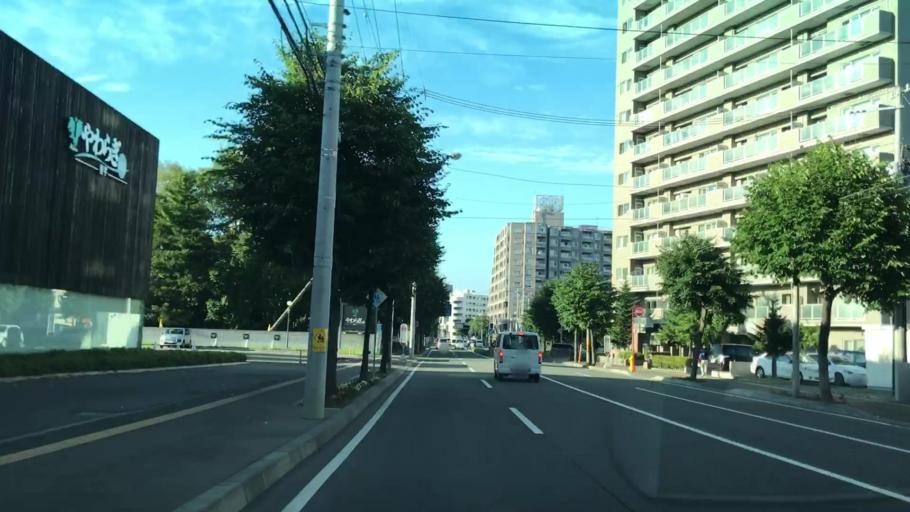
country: JP
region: Hokkaido
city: Sapporo
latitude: 43.0471
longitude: 141.3643
